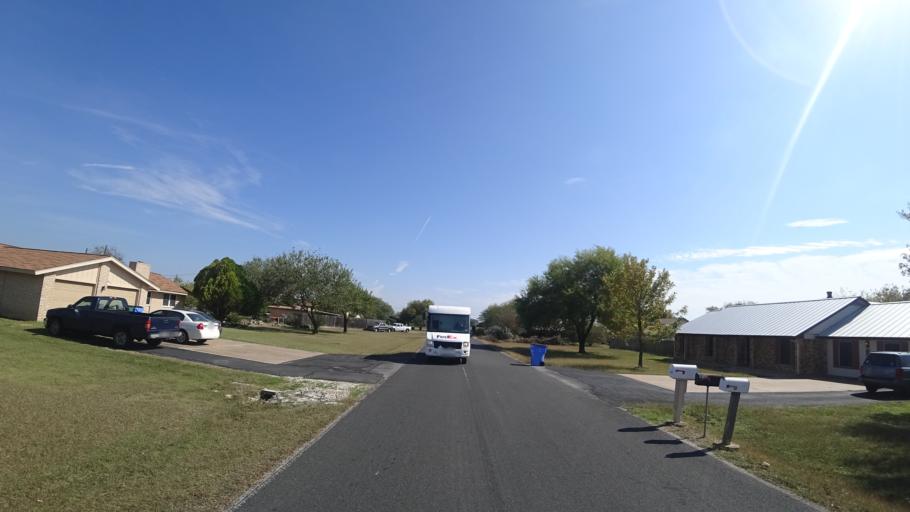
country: US
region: Texas
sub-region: Travis County
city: Pflugerville
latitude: 30.4148
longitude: -97.6258
